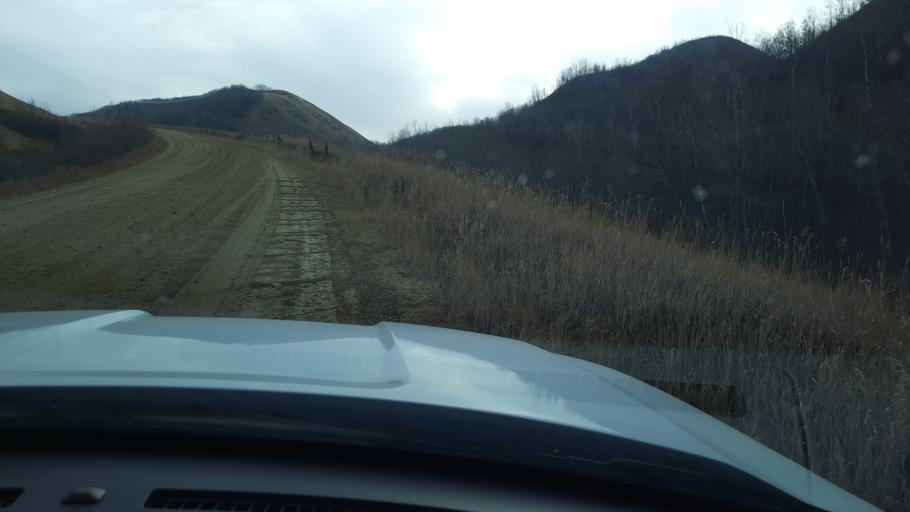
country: CA
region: Saskatchewan
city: White City
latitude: 50.7728
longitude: -104.1334
